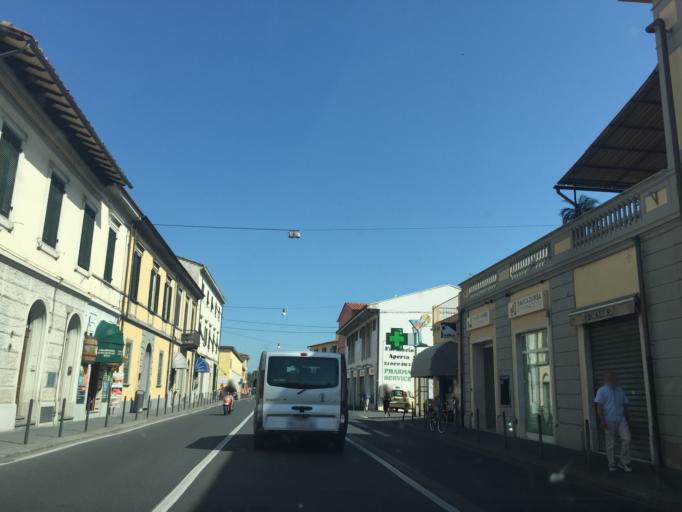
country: IT
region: Tuscany
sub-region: Province of Pisa
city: Pisa
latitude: 43.7230
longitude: 10.3922
